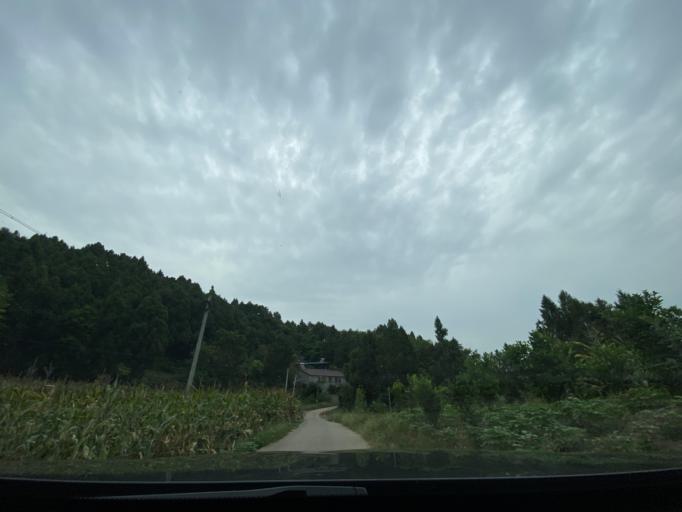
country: CN
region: Sichuan
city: Jiancheng
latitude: 30.3860
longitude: 104.4830
